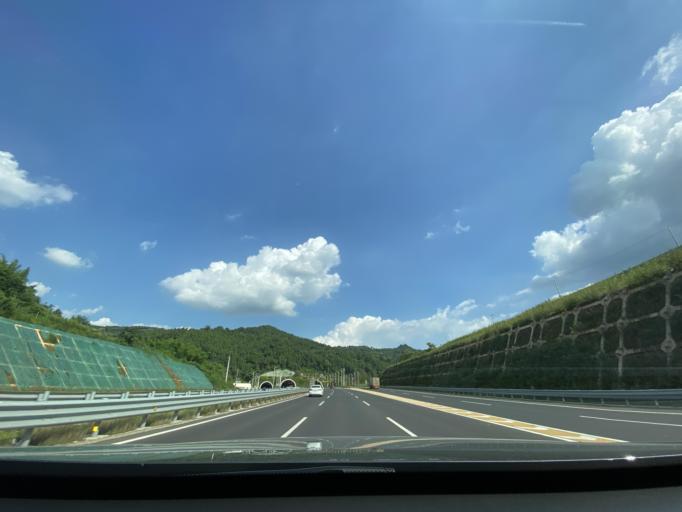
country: CN
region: Sichuan
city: Longquan
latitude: 30.4465
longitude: 104.2399
